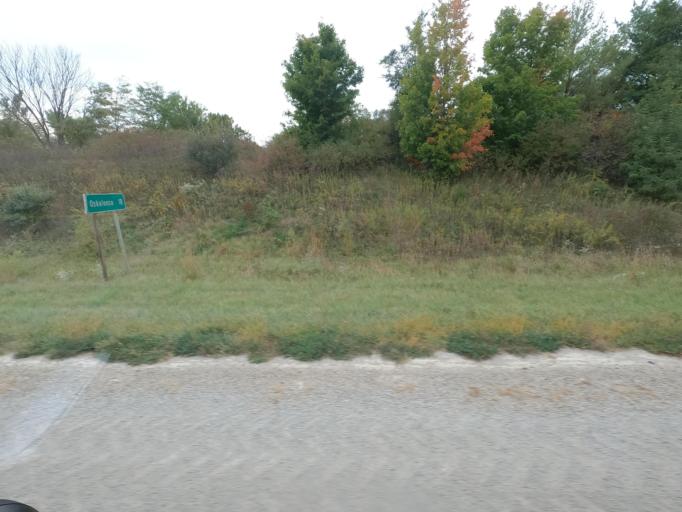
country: US
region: Iowa
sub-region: Marion County
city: Pella
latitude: 41.4041
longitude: -92.9405
